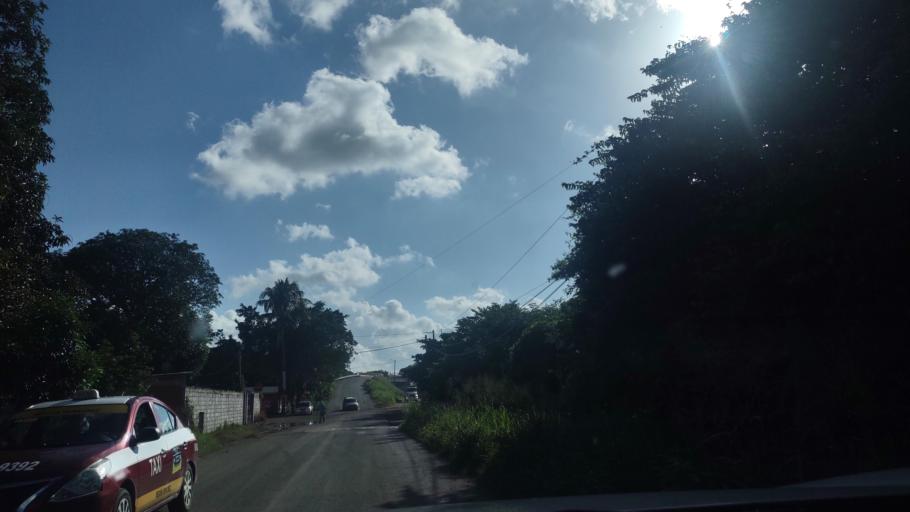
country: MX
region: Veracruz
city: El Tejar
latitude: 19.0660
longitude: -96.1751
